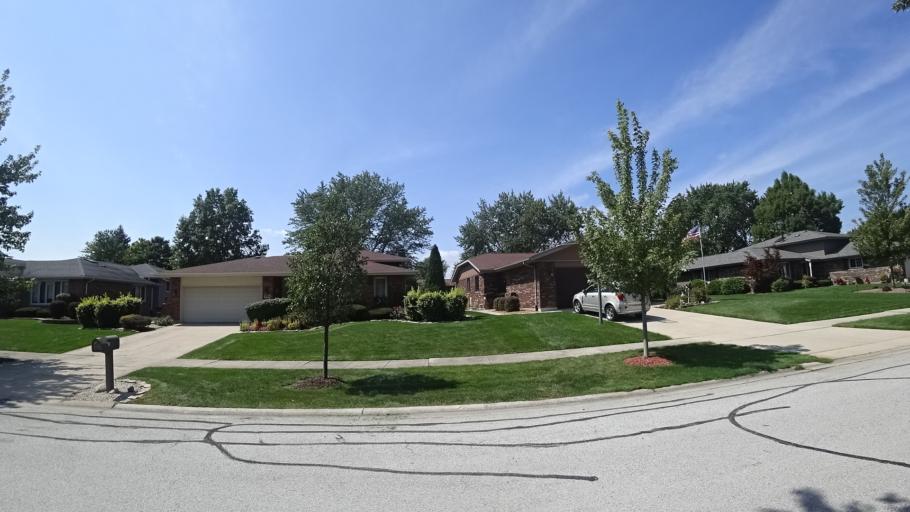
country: US
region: Illinois
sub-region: Cook County
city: Orland Hills
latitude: 41.5702
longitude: -87.8402
